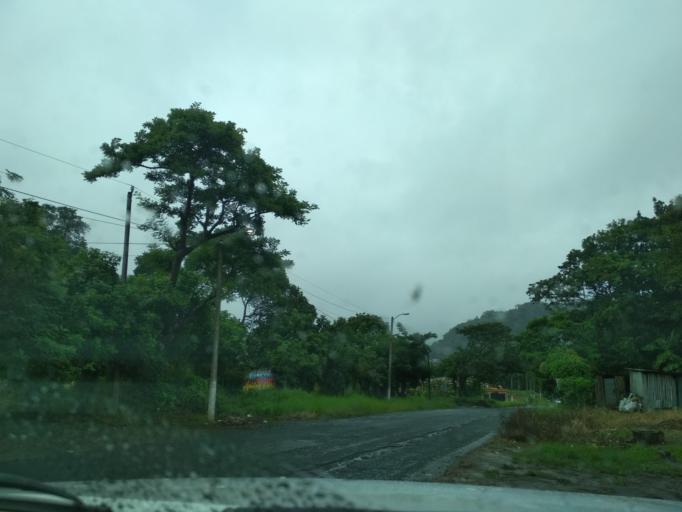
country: MX
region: Veracruz
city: Santiago Tuxtla
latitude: 18.4626
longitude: -95.2942
